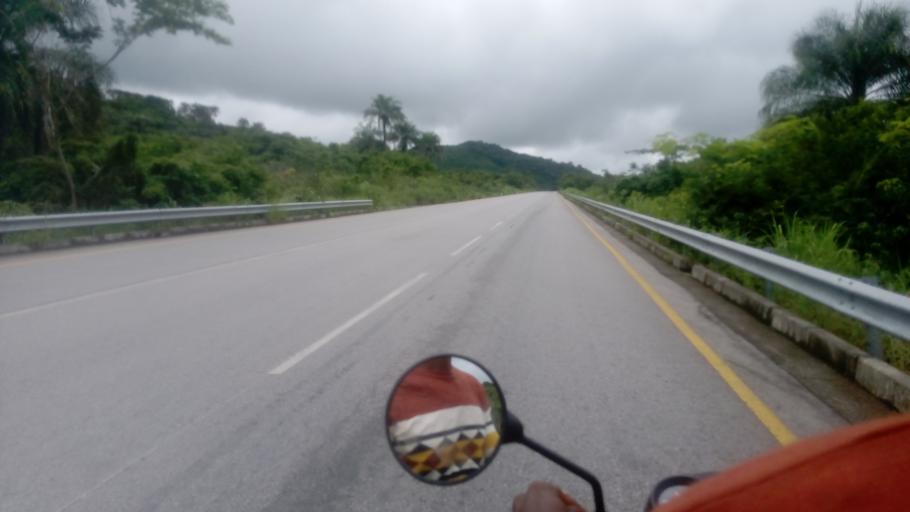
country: SL
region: Northern Province
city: Masaka
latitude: 8.6616
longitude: -11.7904
